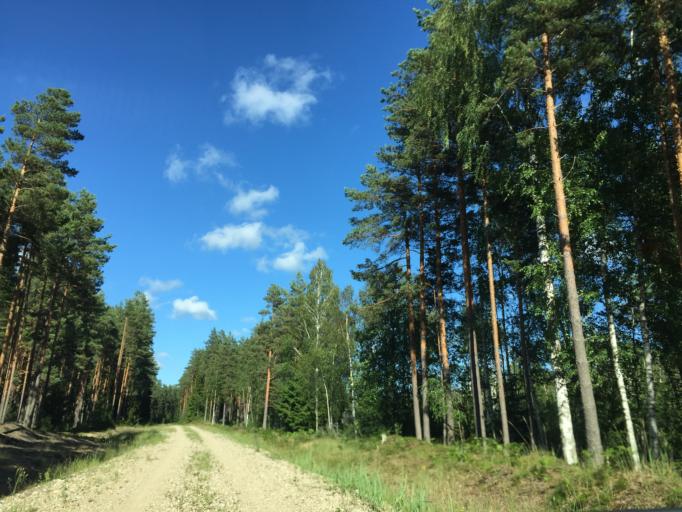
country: LV
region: Ventspils
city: Ventspils
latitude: 57.5427
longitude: 21.7592
